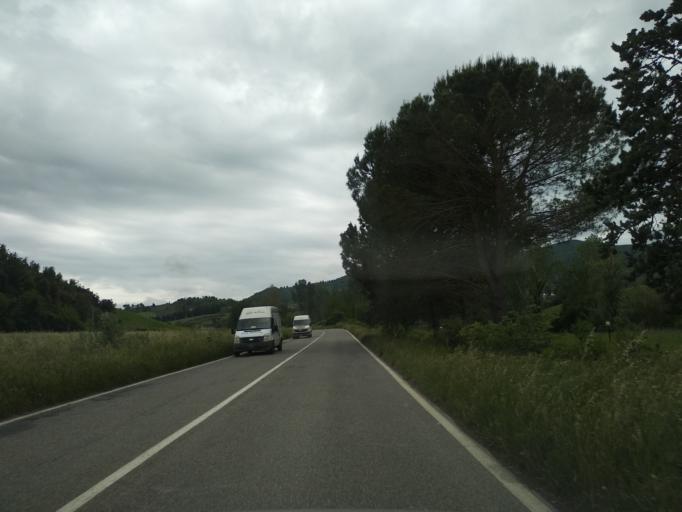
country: IT
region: Tuscany
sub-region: Provincia di Livorno
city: Collesalvetti
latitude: 43.5340
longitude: 10.4616
